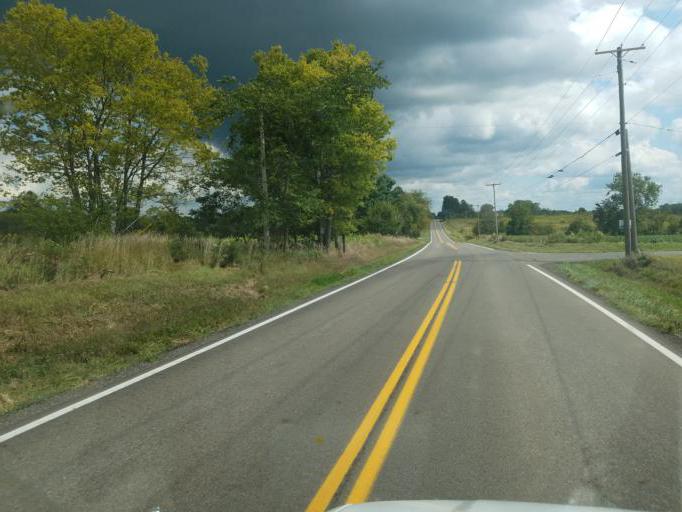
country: US
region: Ohio
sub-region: Huron County
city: Greenwich
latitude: 40.9172
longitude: -82.5136
